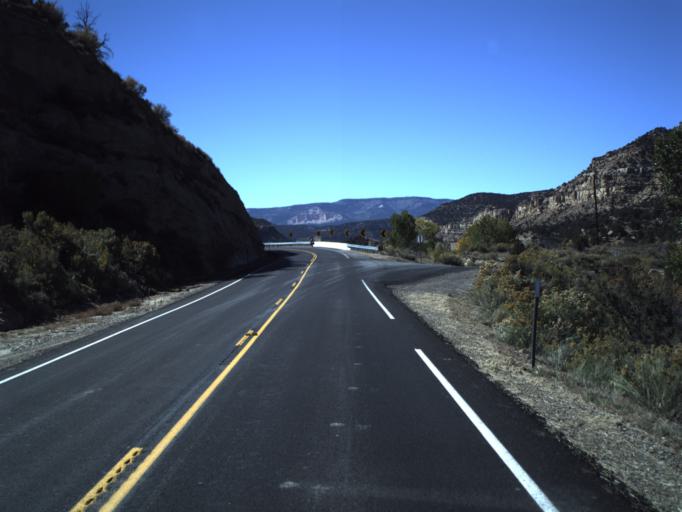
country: US
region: Utah
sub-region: Wayne County
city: Loa
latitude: 37.7649
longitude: -111.6823
